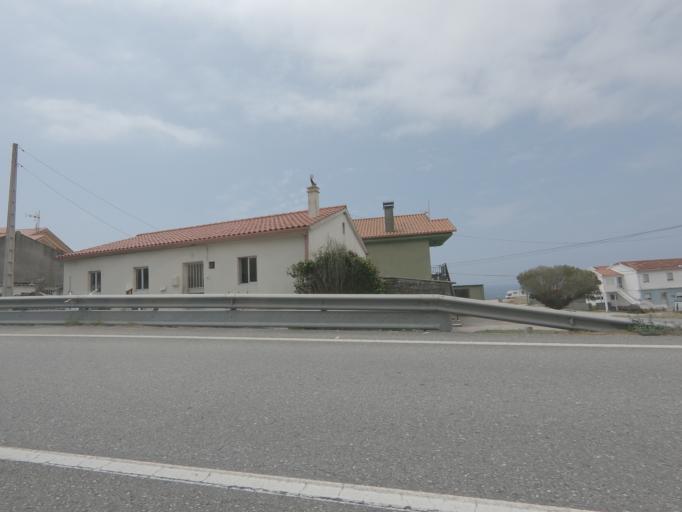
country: ES
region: Galicia
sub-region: Provincia de Pontevedra
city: O Rosal
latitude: 41.9499
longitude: -8.8832
